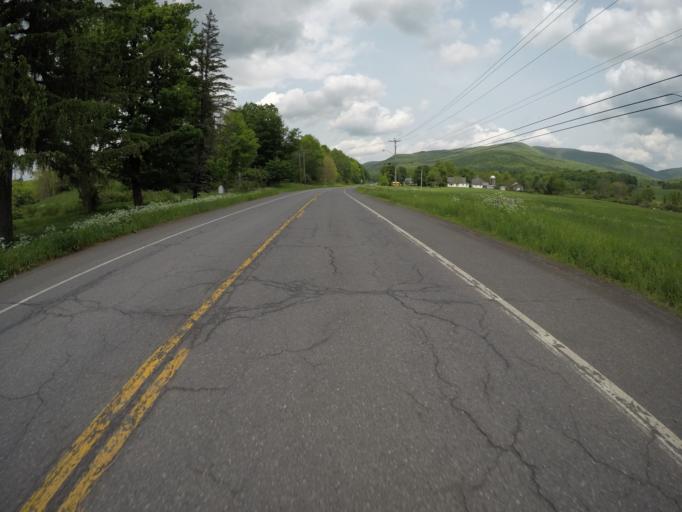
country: US
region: New York
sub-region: Delaware County
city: Stamford
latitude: 42.2967
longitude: -74.5581
